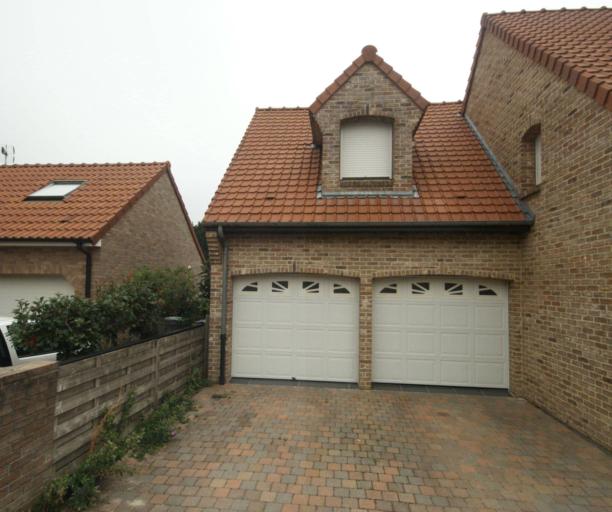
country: FR
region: Nord-Pas-de-Calais
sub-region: Departement du Nord
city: Willems
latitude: 50.6198
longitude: 3.2349
